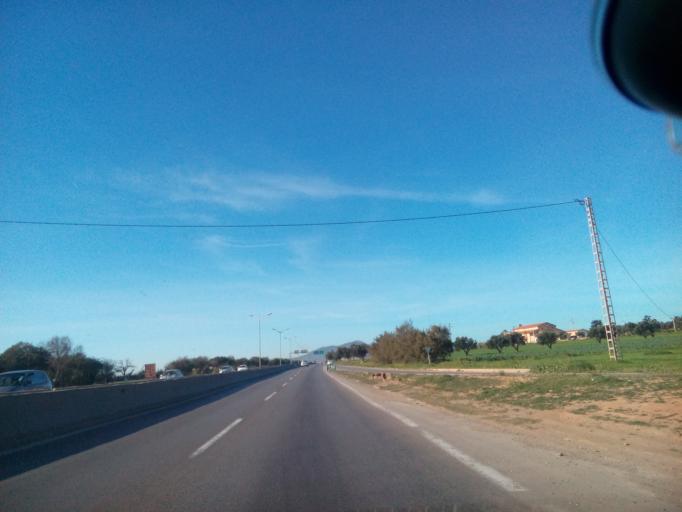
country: DZ
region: Oran
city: Ain el Bya
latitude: 35.7950
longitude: -0.3855
